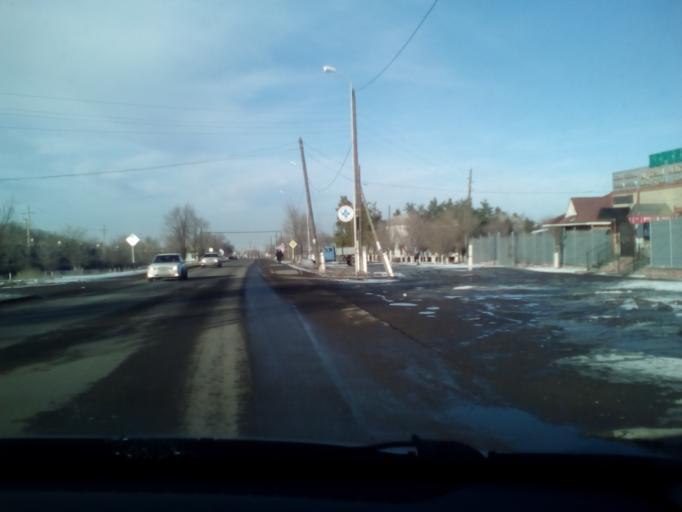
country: KZ
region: Almaty Oblysy
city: Burunday
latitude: 43.1839
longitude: 76.4145
